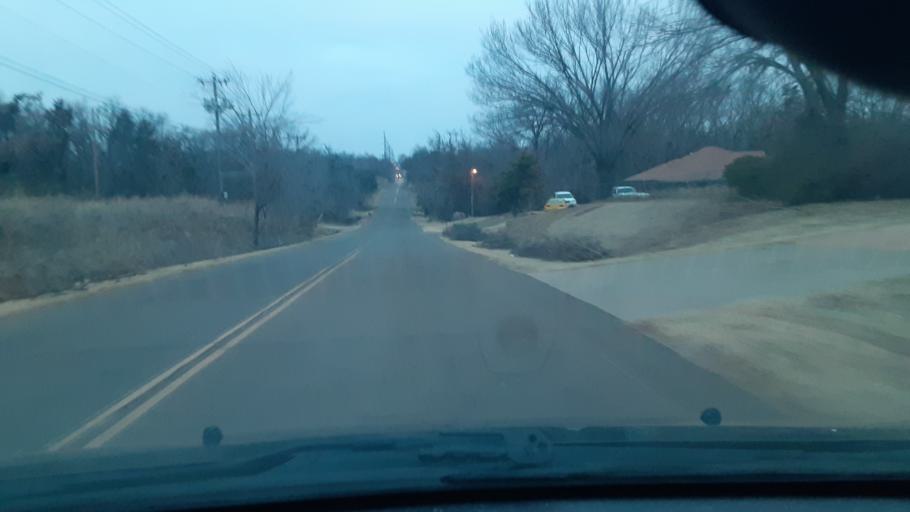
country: US
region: Oklahoma
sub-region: Logan County
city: Guthrie
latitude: 35.8678
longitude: -97.4075
